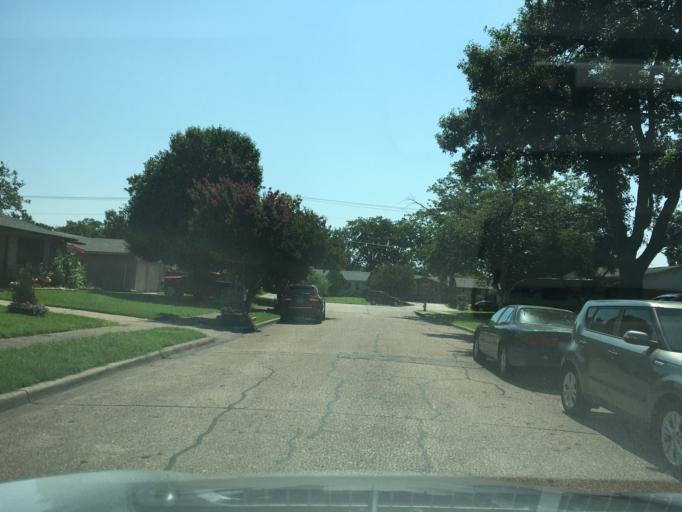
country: US
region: Texas
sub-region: Dallas County
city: Richardson
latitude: 32.9202
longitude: -96.6934
